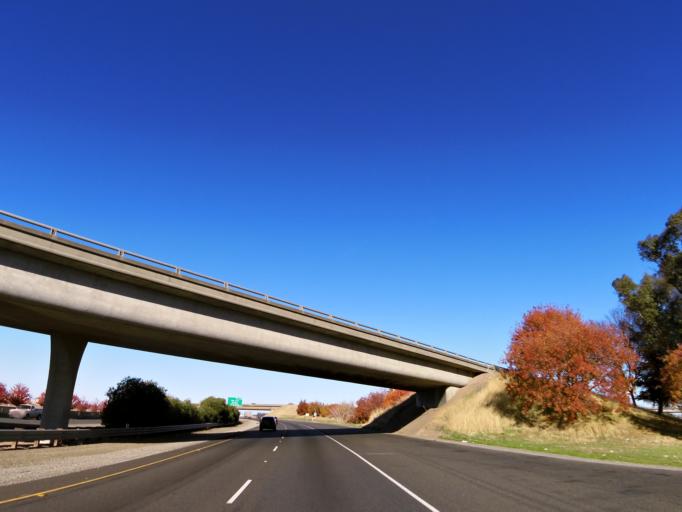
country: US
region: California
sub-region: Yolo County
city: West Sacramento
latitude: 38.6673
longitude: -121.5397
